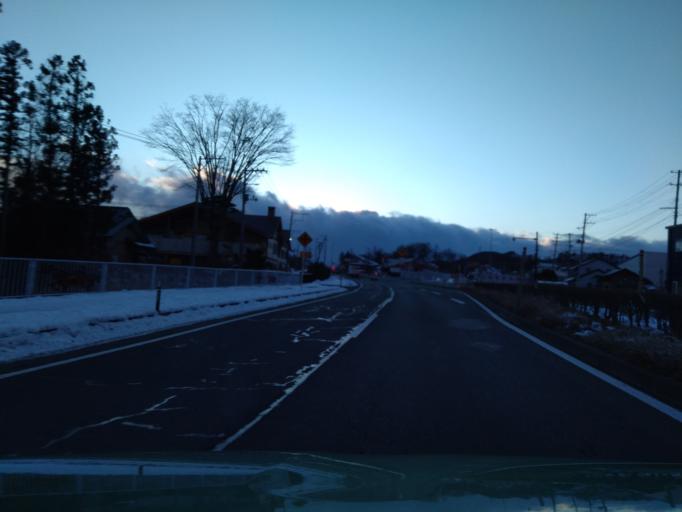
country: JP
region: Iwate
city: Shizukuishi
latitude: 39.7017
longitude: 141.0307
